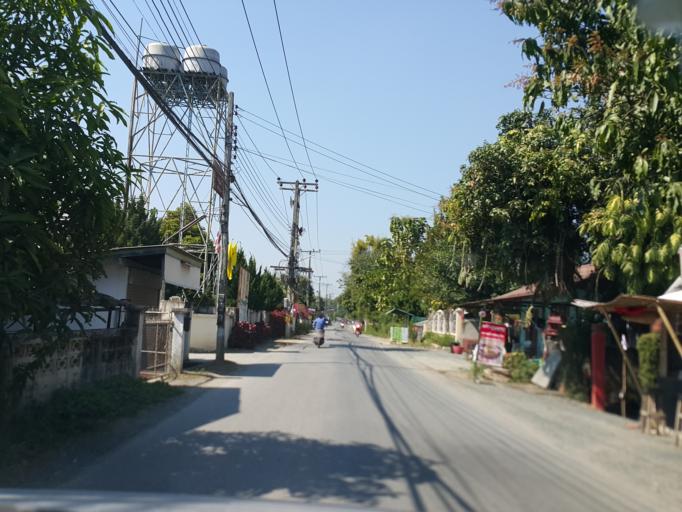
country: TH
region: Chiang Mai
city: San Kamphaeng
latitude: 18.7394
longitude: 99.1061
